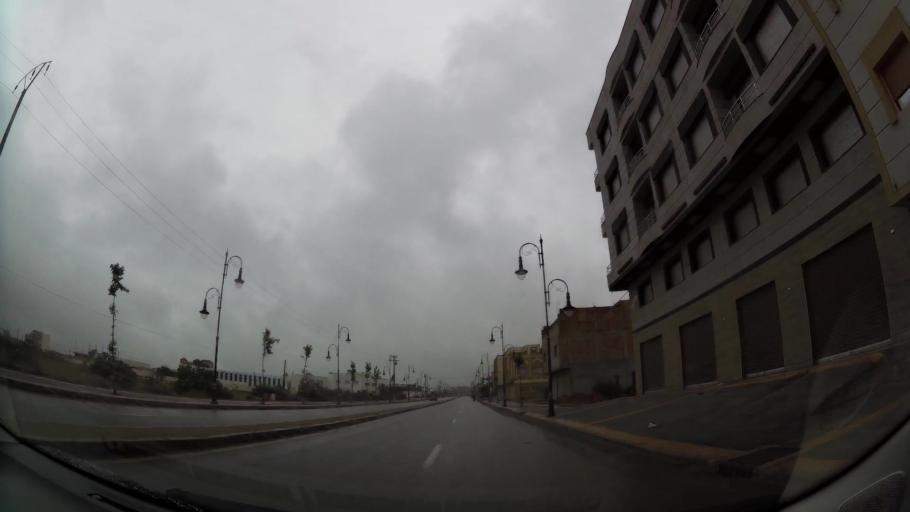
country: MA
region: Taza-Al Hoceima-Taounate
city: Imzourene
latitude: 35.1675
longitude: -3.8578
